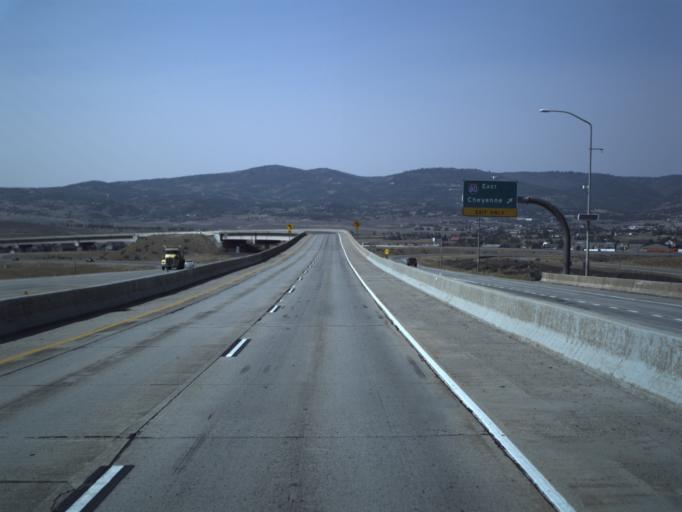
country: US
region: Utah
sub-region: Summit County
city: Snyderville
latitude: 40.7269
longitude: -111.4939
